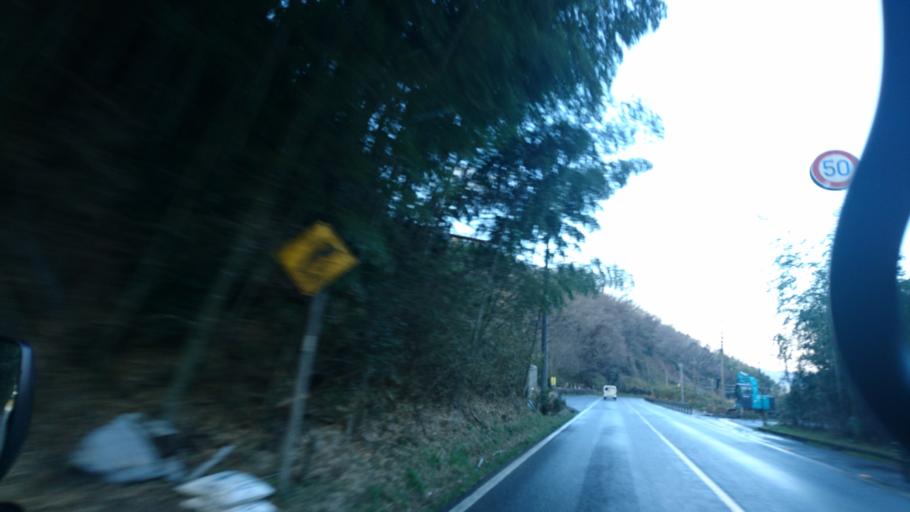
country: JP
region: Mie
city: Ueno-ebisumachi
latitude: 34.7620
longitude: 136.0963
